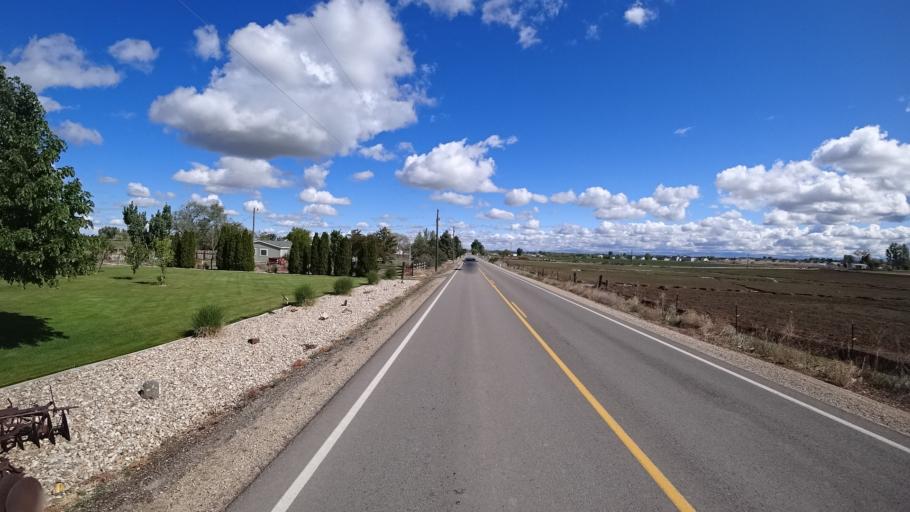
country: US
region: Idaho
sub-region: Ada County
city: Kuna
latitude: 43.4976
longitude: -116.4537
